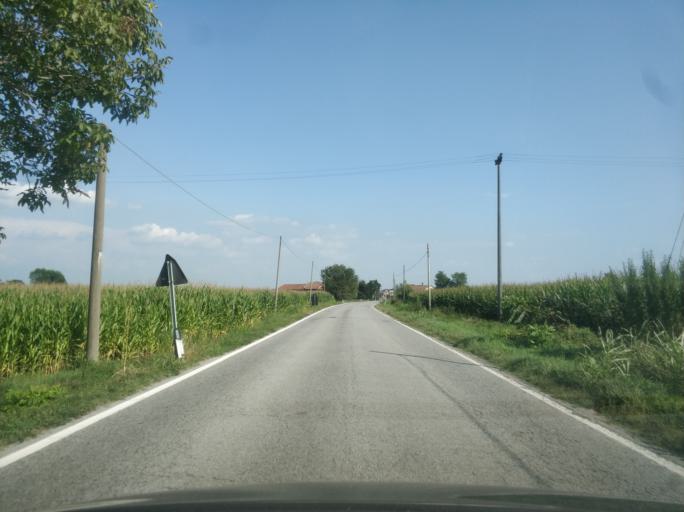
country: IT
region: Piedmont
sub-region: Provincia di Cuneo
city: Centallo
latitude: 44.5358
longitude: 7.6238
